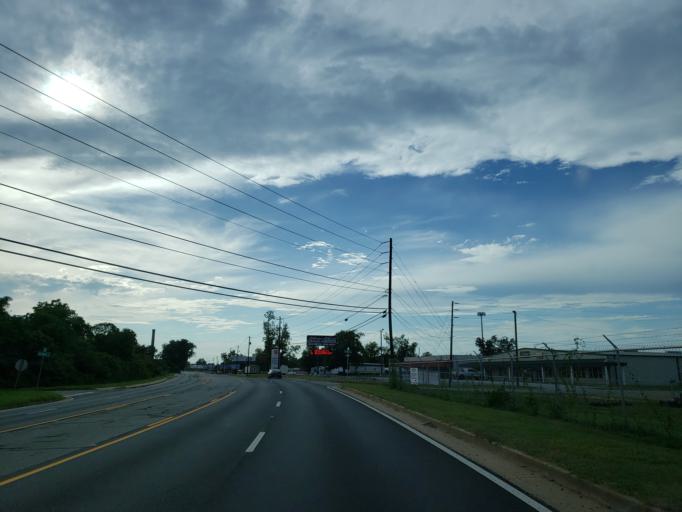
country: US
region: Georgia
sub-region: Tift County
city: Tifton
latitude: 31.4481
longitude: -83.4917
